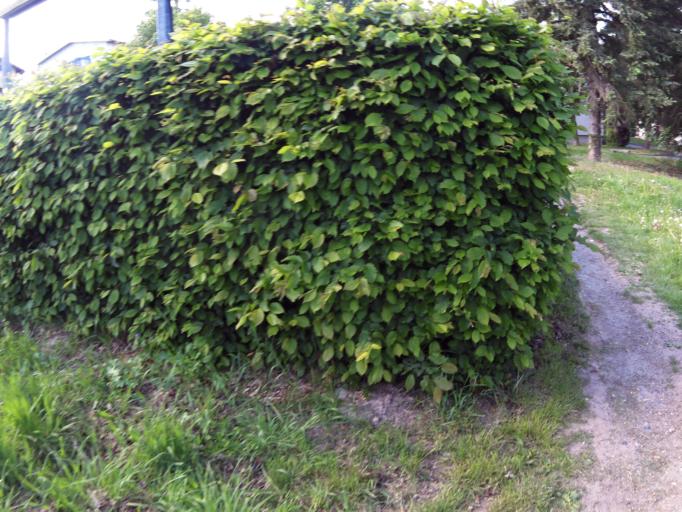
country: DE
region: Thuringia
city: Bad Salzungen
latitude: 50.8060
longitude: 10.2178
